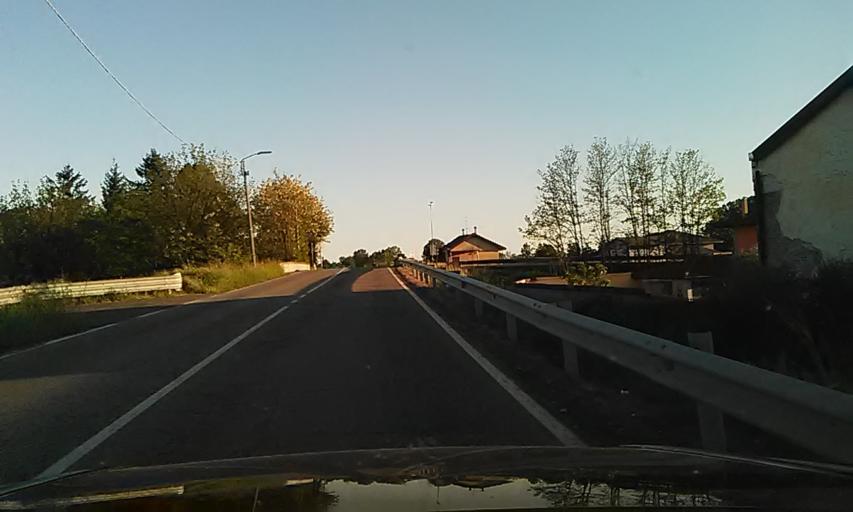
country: IT
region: Piedmont
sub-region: Provincia di Vercelli
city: Ghislarengo
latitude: 45.5256
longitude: 8.3861
